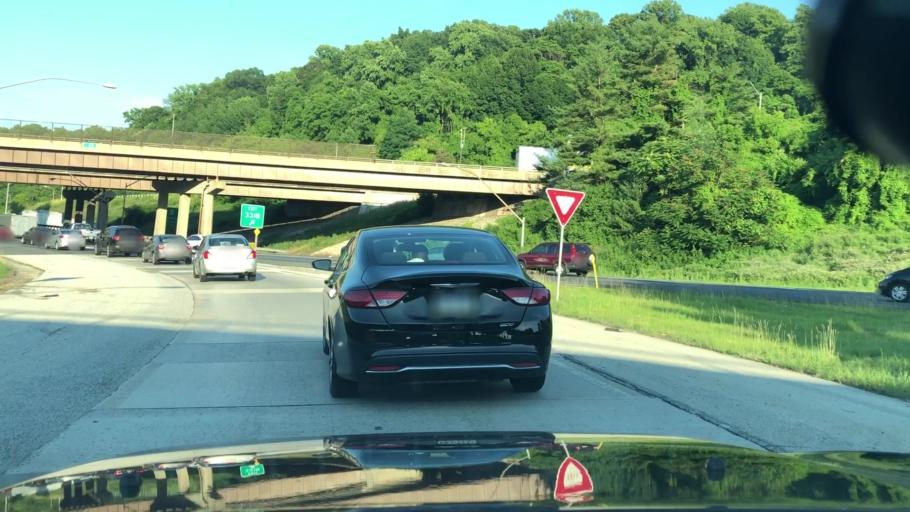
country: US
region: Pennsylvania
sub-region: Montgomery County
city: West Conshohocken
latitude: 40.0643
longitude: -75.3231
